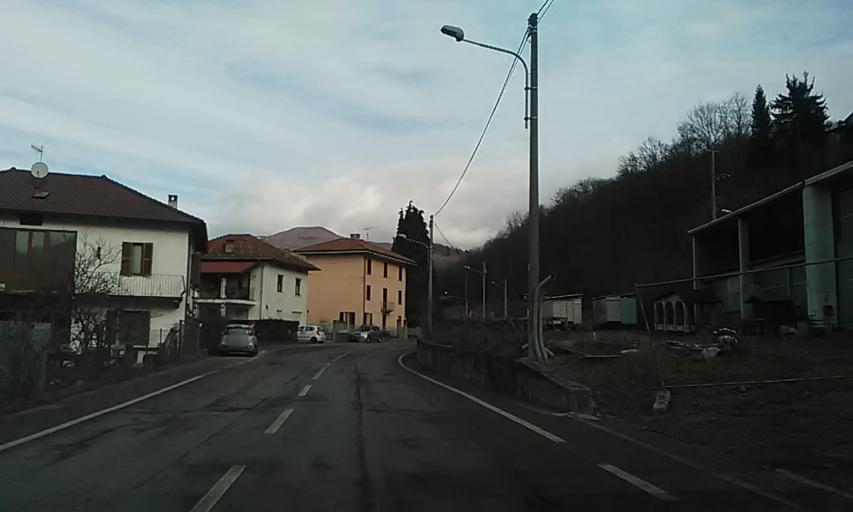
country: IT
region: Piedmont
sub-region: Provincia di Vercelli
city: Borgosesia
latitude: 45.7236
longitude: 8.2835
